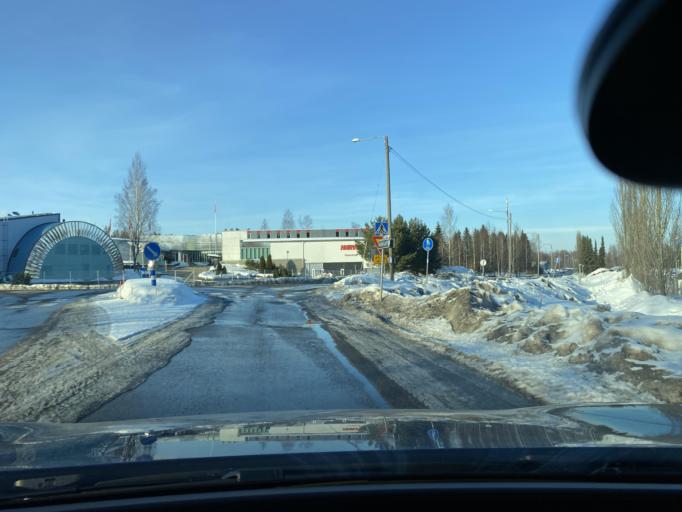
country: FI
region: Central Finland
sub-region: Jyvaeskylae
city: Muurame
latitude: 62.1022
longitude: 25.6483
